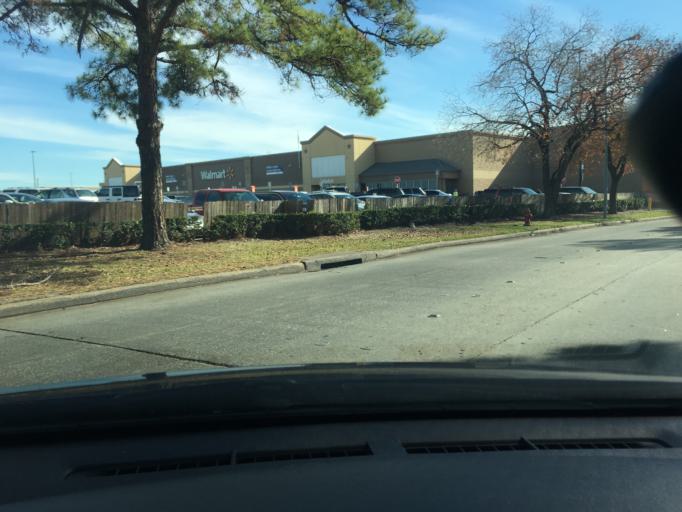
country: US
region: Texas
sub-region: Harris County
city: Cloverleaf
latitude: 29.8071
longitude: -95.1663
